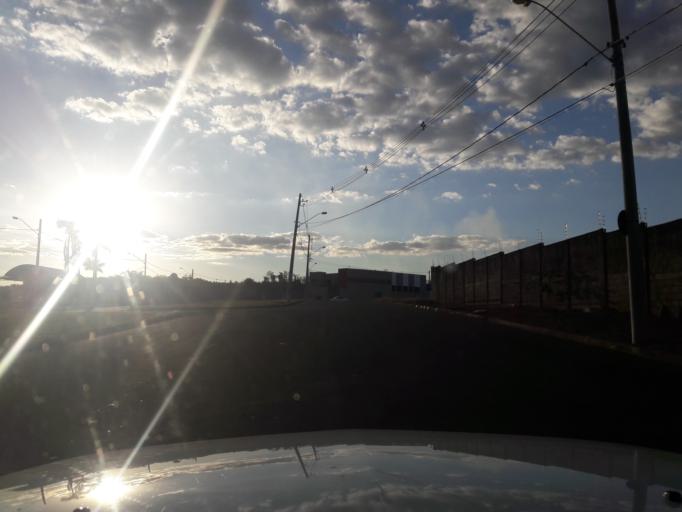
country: BR
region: Sao Paulo
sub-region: Moji-Guacu
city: Mogi-Gaucu
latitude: -22.3939
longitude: -46.9511
